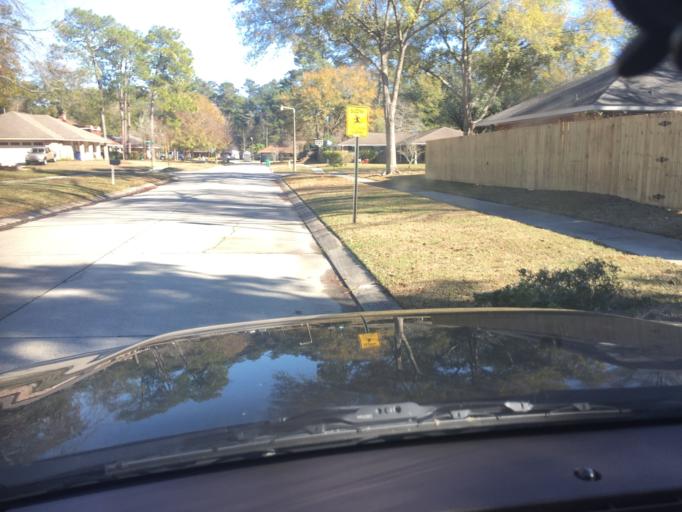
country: US
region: Louisiana
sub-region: Saint Tammany Parish
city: Slidell
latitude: 30.3043
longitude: -89.7471
